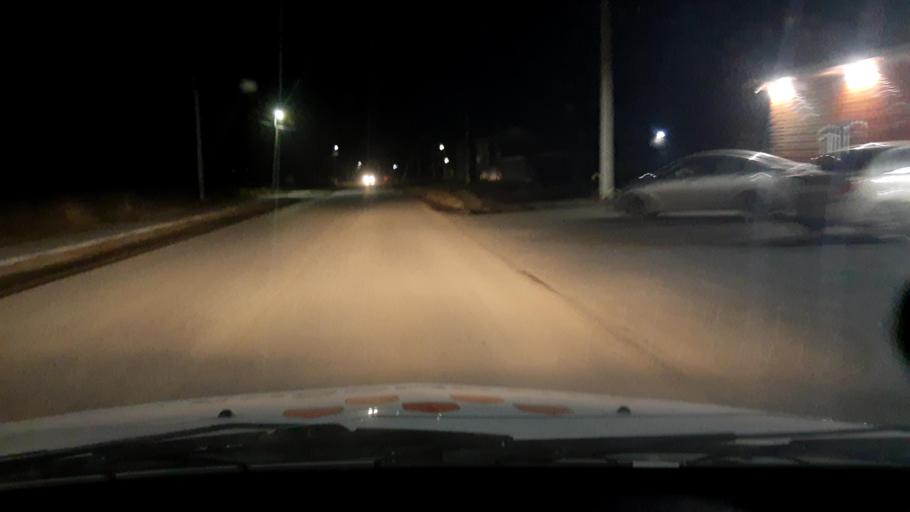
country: RU
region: Bashkortostan
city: Iglino
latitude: 54.7902
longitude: 56.2665
